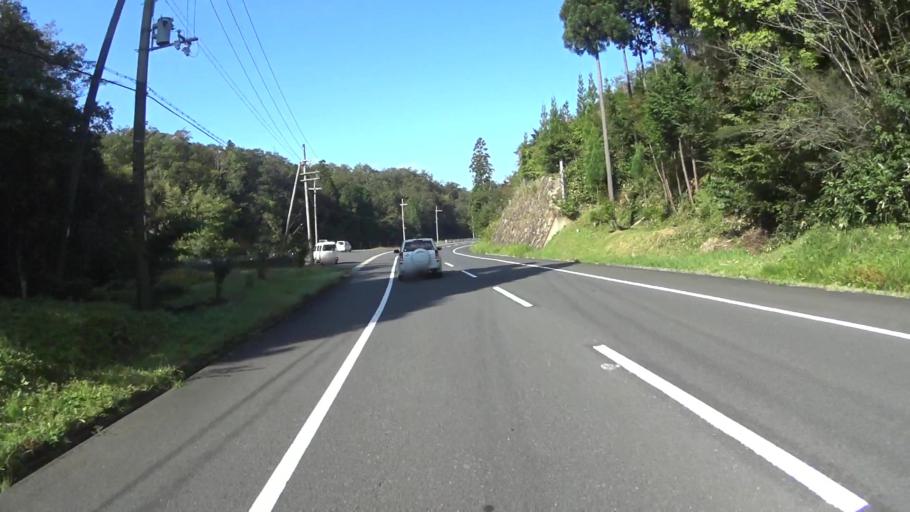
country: JP
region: Kyoto
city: Miyazu
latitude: 35.5939
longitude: 135.1476
